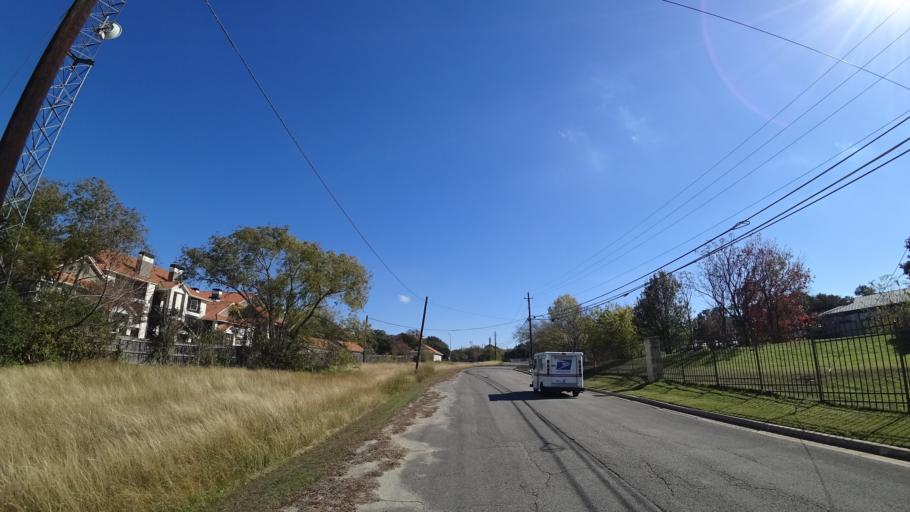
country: US
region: Texas
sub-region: Travis County
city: Wells Branch
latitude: 30.4336
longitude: -97.6975
